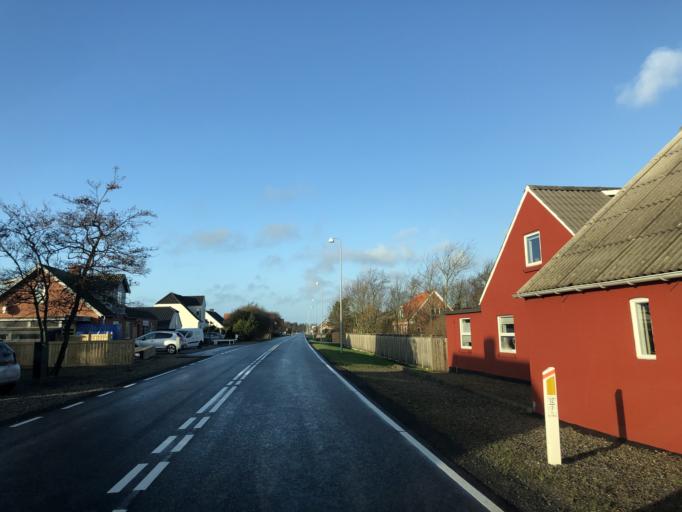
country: DK
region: Central Jutland
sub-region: Struer Kommune
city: Struer
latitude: 56.5490
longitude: 8.4887
